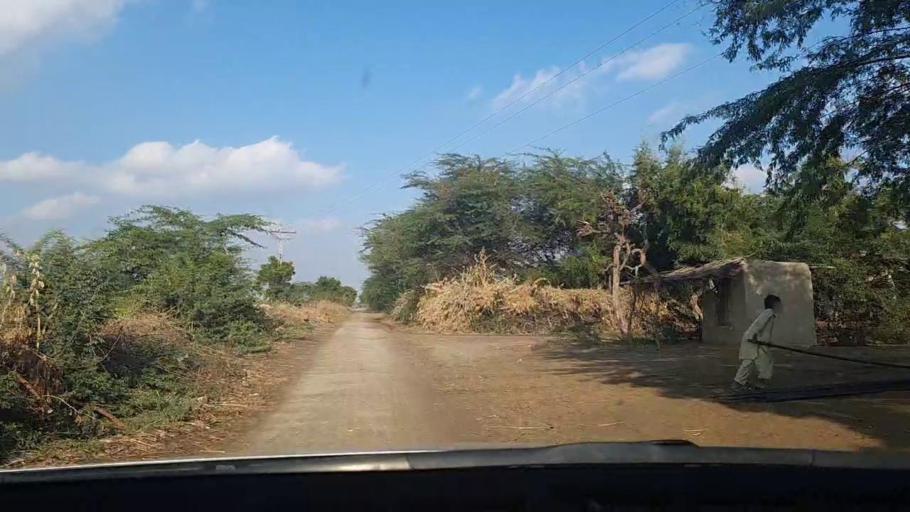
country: PK
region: Sindh
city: Tando Mittha Khan
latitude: 25.8843
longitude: 69.2968
